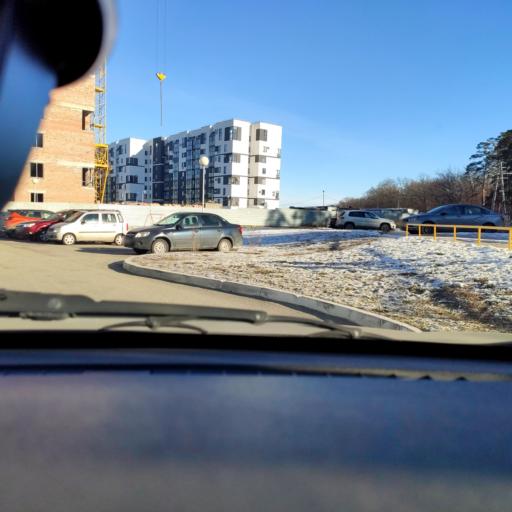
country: RU
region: Samara
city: Tol'yatti
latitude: 53.5248
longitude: 49.3381
